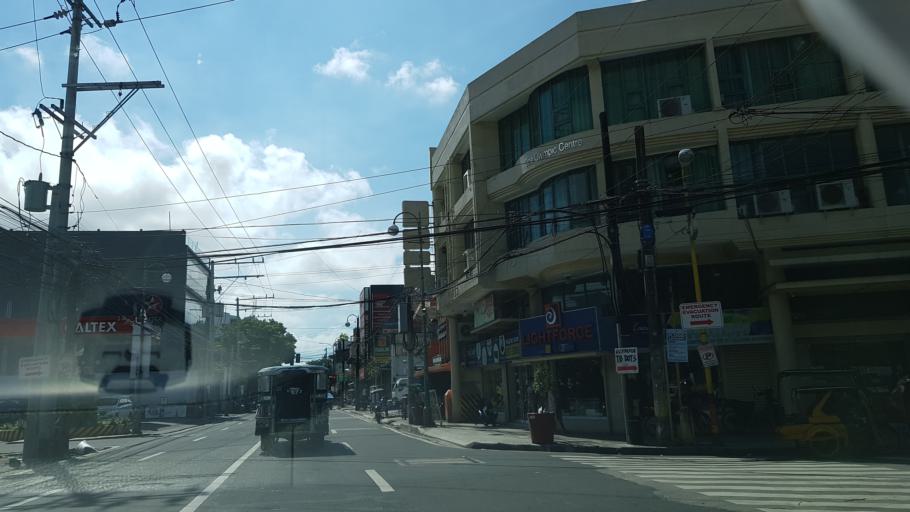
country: PH
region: Metro Manila
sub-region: Mandaluyong
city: Mandaluyong City
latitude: 14.5710
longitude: 121.0201
